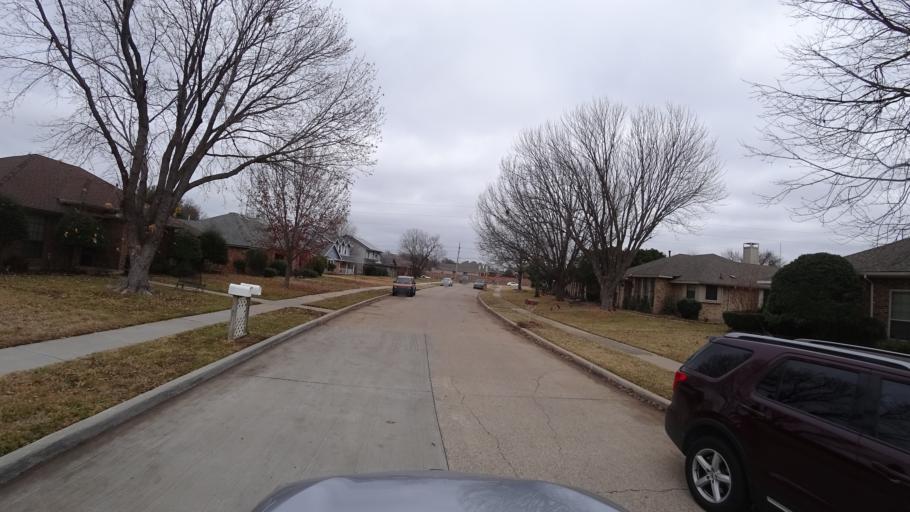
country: US
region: Texas
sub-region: Denton County
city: Lewisville
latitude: 33.0463
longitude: -97.0373
